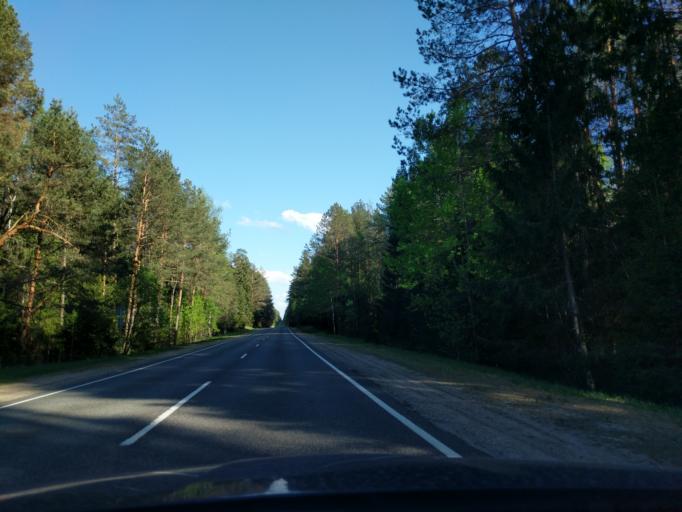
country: BY
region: Minsk
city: Myadzyel
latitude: 54.8065
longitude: 26.9898
